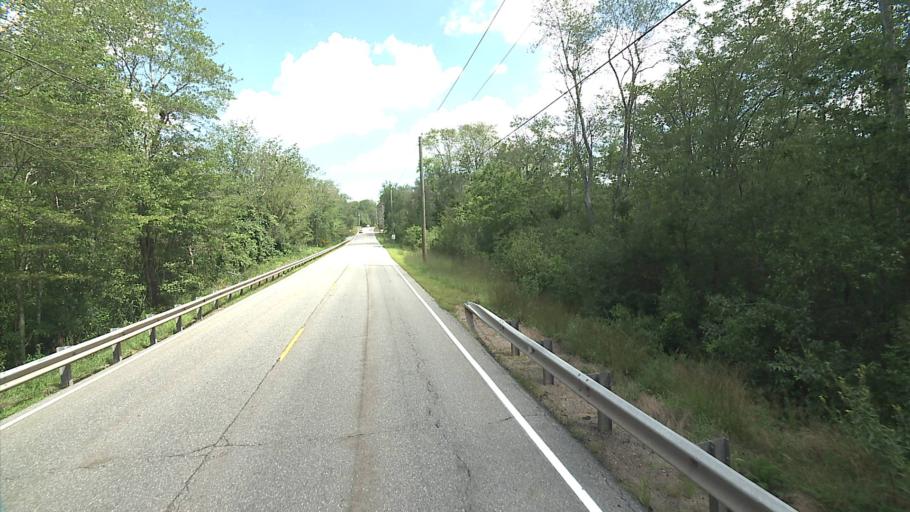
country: US
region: Connecticut
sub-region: Windham County
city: Windham
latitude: 41.7970
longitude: -72.1258
